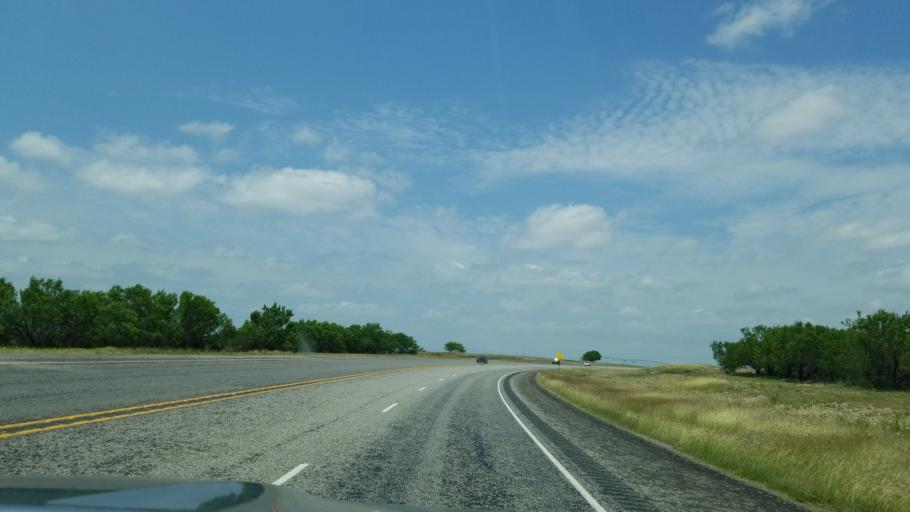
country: US
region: Texas
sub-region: Zavala County
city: La Pryor
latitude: 28.9321
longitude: -99.8029
